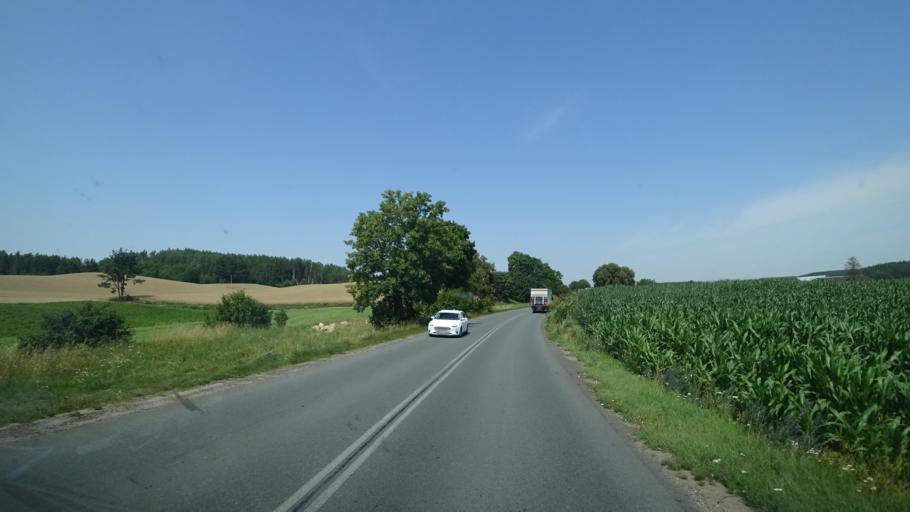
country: PL
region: Pomeranian Voivodeship
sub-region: Powiat koscierski
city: Lipusz
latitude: 54.0722
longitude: 17.8027
